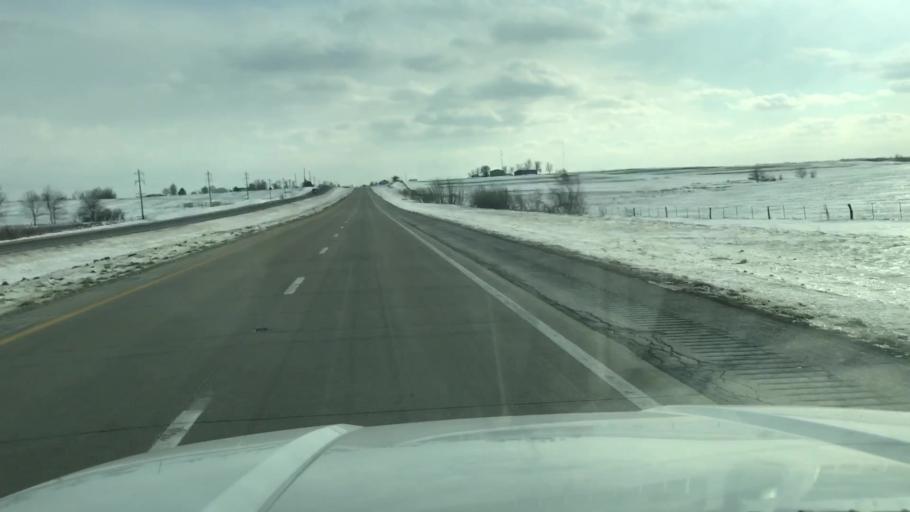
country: US
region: Missouri
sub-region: Nodaway County
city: Maryville
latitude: 40.2676
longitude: -94.8669
